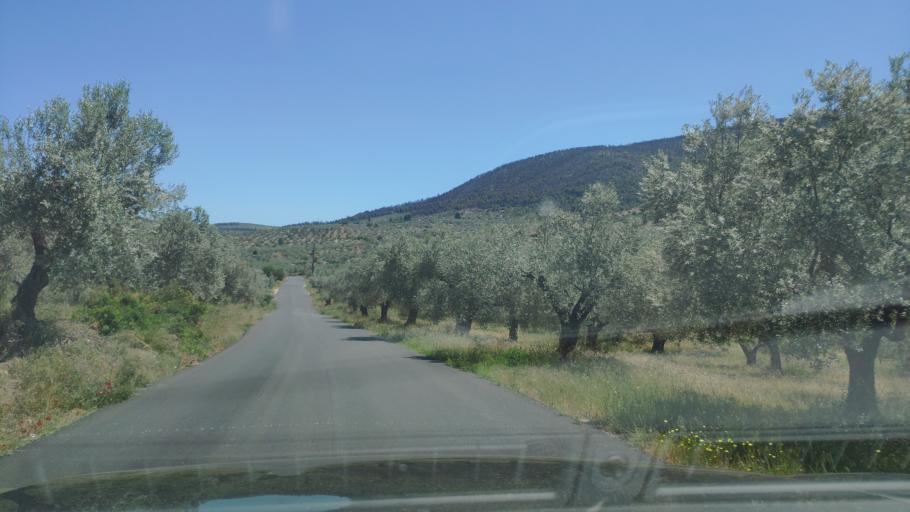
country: GR
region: Peloponnese
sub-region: Nomos Korinthias
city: Athikia
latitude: 37.8064
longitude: 22.9104
